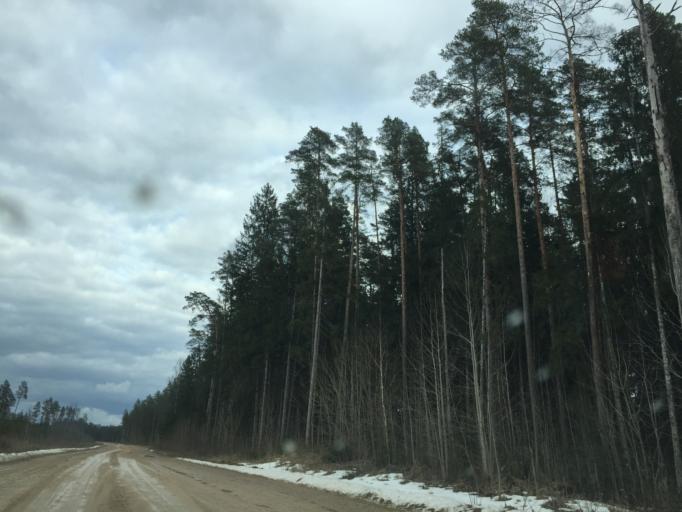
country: LV
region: Lielvarde
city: Lielvarde
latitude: 56.5327
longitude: 24.8129
